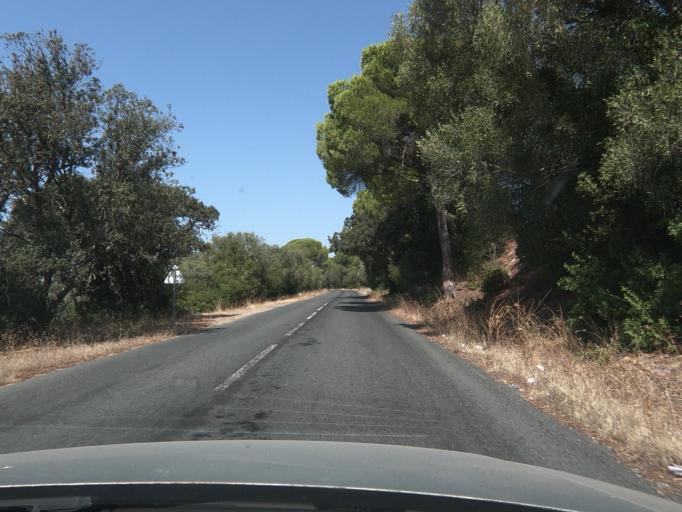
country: PT
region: Setubal
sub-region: Alcacer do Sal
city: Alcacer do Sal
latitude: 38.2921
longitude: -8.4035
